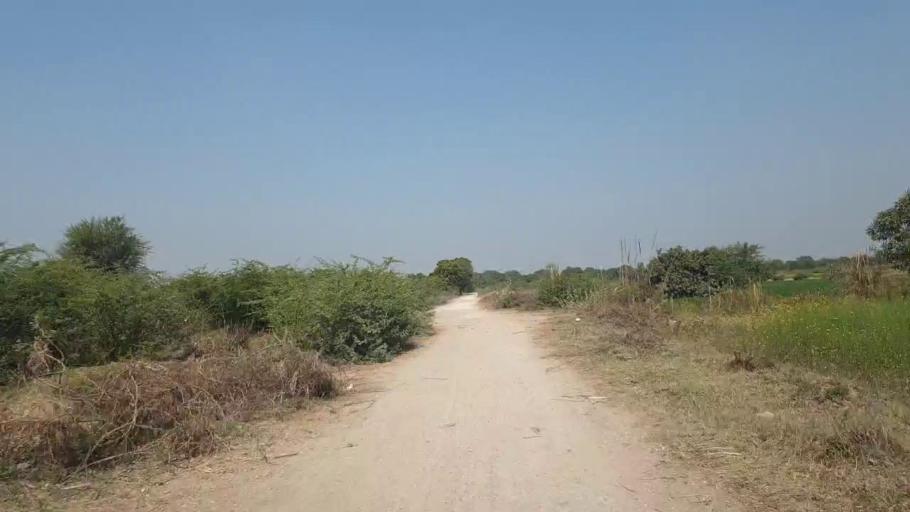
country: PK
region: Sindh
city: Chambar
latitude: 25.4128
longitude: 68.9069
